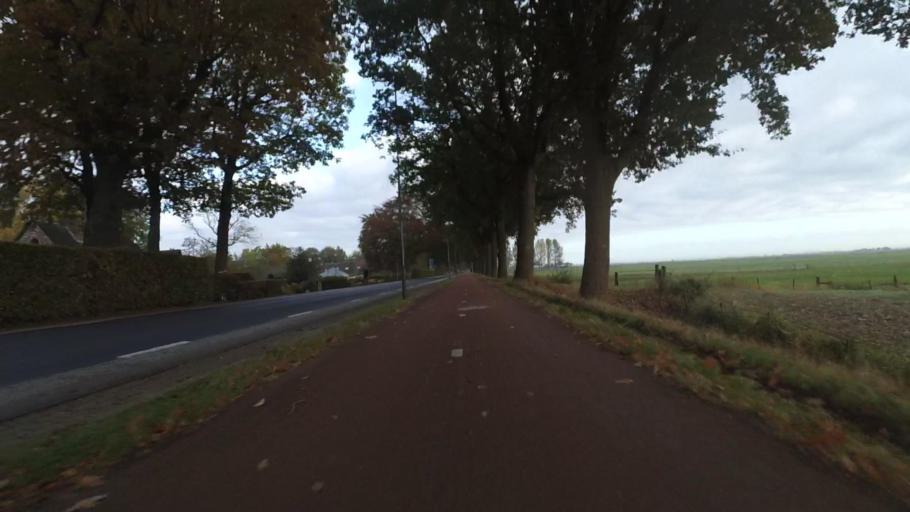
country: NL
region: Utrecht
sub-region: Gemeente Baarn
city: Baarn
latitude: 52.2338
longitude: 5.2595
